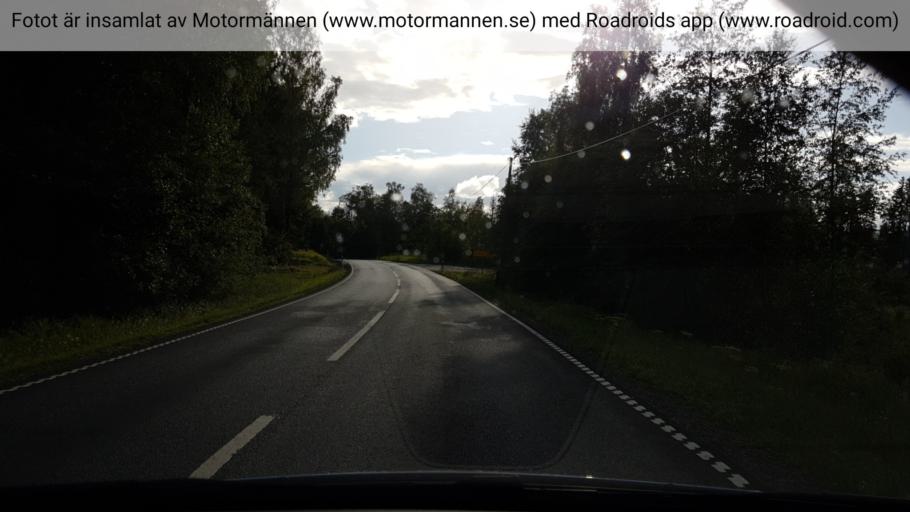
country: SE
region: OErebro
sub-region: Hallefors Kommun
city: Haellefors
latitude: 59.8050
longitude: 14.5945
